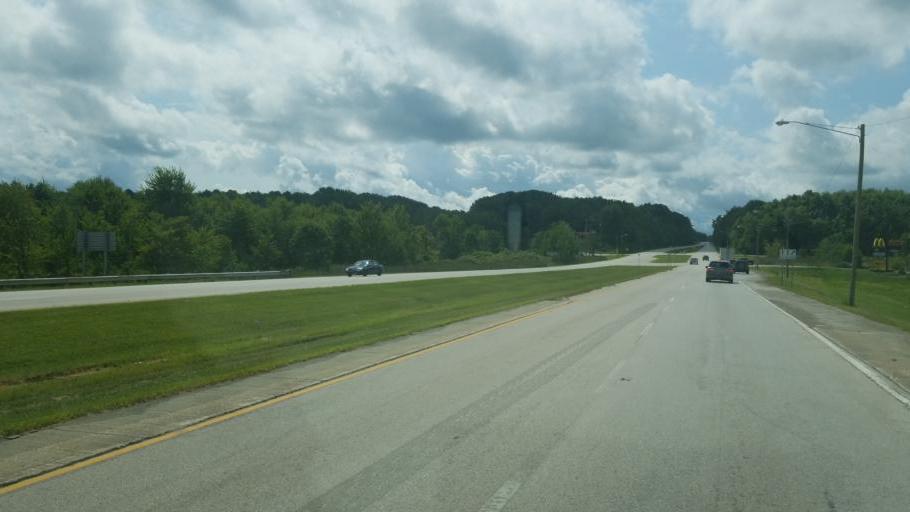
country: US
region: Ohio
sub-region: Ashtabula County
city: Conneaut
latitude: 41.9151
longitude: -80.5689
